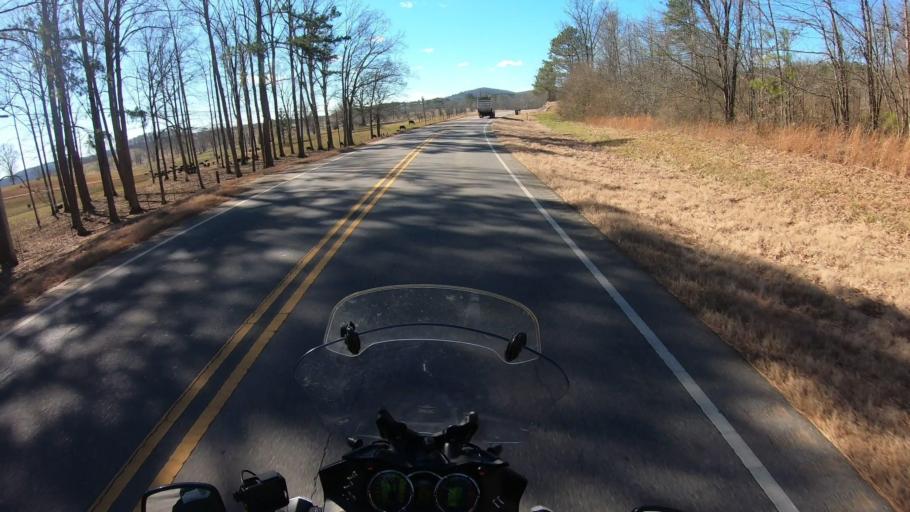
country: US
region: Alabama
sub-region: Cleburne County
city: Heflin
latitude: 33.5327
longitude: -85.6230
